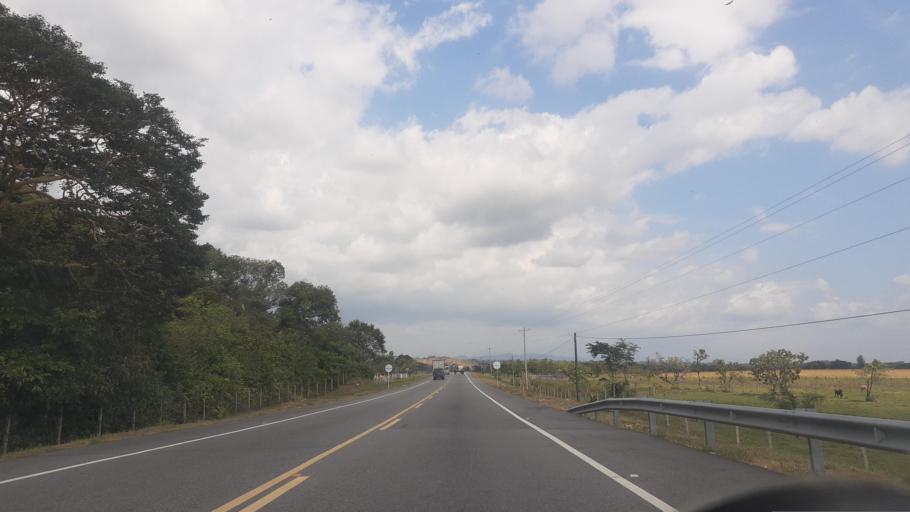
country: CO
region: Casanare
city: Tauramena
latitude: 4.9074
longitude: -72.6758
